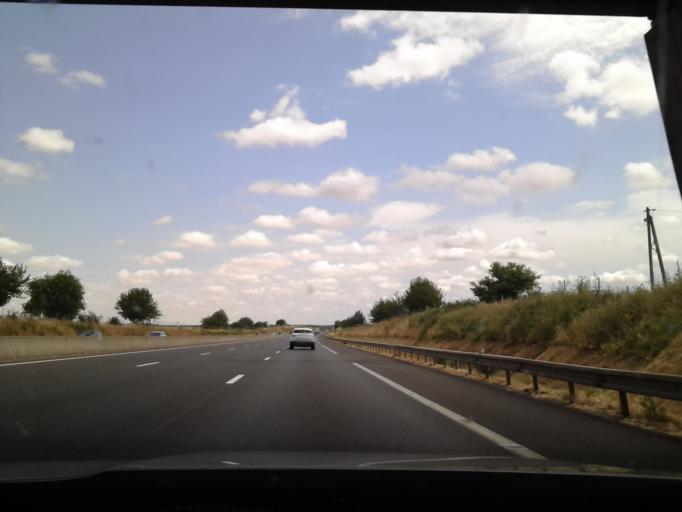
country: FR
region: Centre
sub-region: Departement d'Indre-et-Loire
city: Reugny
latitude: 47.5030
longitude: 0.8631
